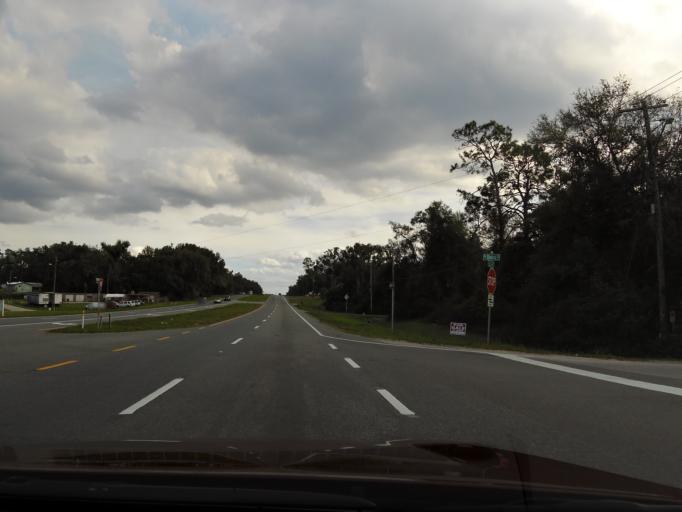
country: US
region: Florida
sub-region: Volusia County
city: De Leon Springs
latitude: 29.1115
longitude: -81.3492
